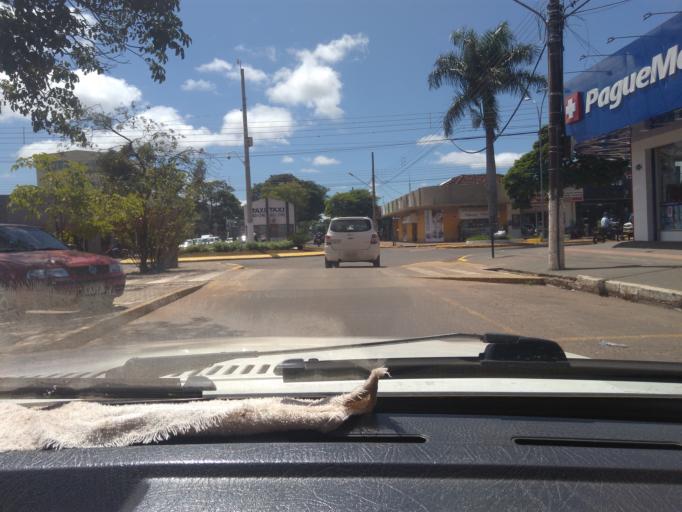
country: BR
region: Mato Grosso do Sul
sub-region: Ponta Pora
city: Ponta Pora
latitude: -22.5387
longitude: -55.7303
